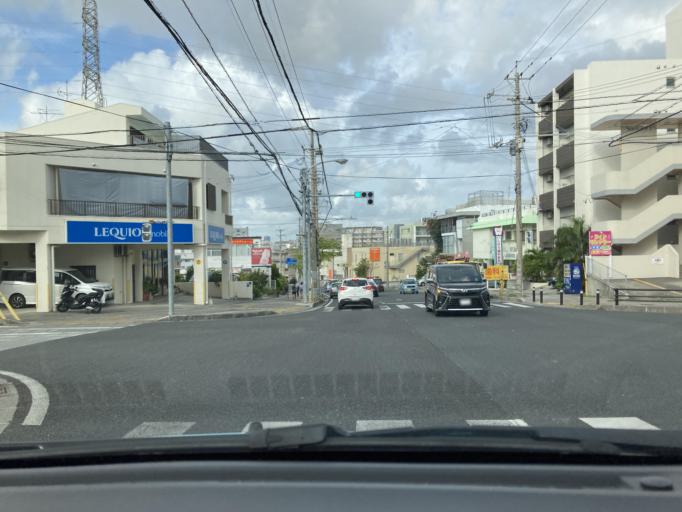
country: JP
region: Okinawa
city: Tomigusuku
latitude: 26.1899
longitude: 127.6743
